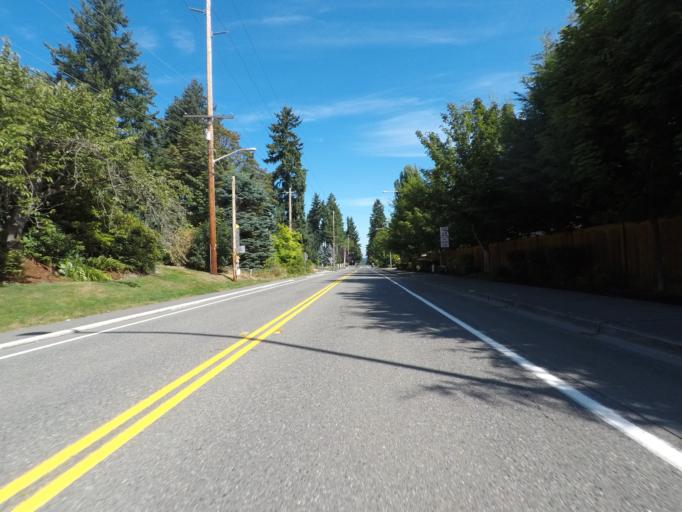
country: US
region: Washington
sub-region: King County
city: Inglewood-Finn Hill
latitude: 47.7386
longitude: -122.2289
